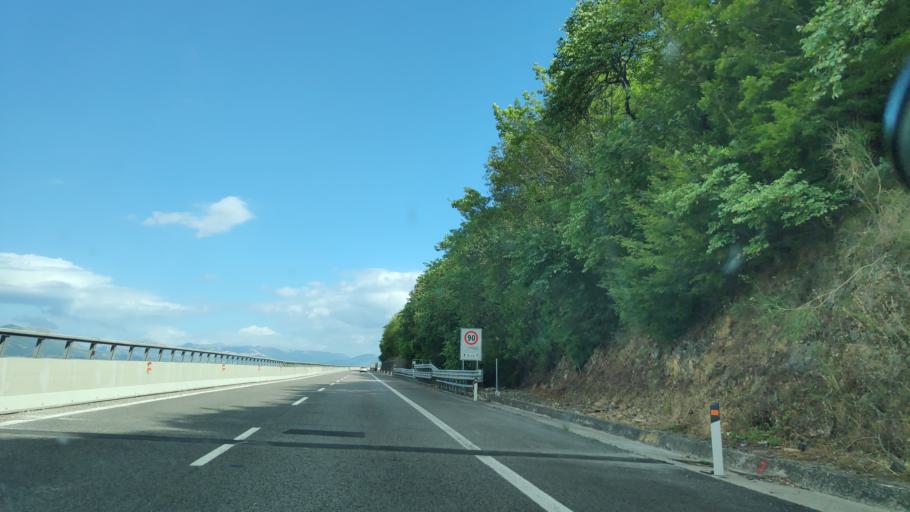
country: IT
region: Campania
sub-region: Provincia di Salerno
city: Sicignano degli Alburni
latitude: 40.5977
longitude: 15.3174
